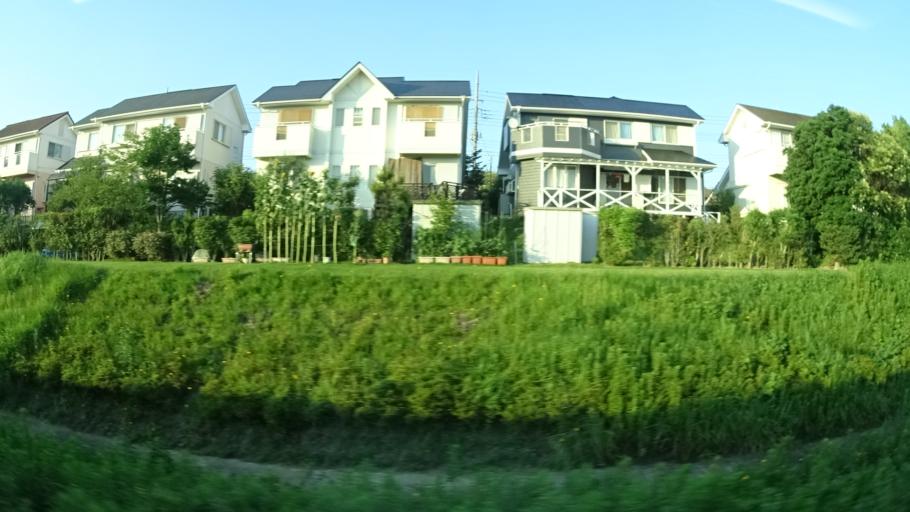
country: JP
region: Ibaraki
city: Ishioka
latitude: 36.1824
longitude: 140.2866
